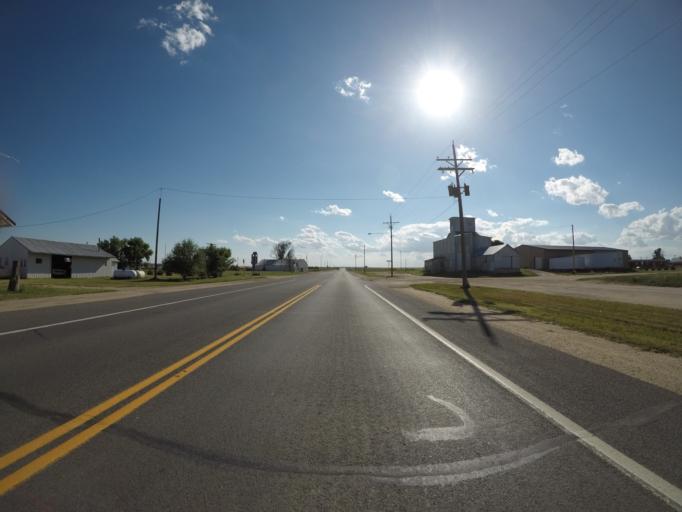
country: US
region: Colorado
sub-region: Morgan County
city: Fort Morgan
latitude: 40.6063
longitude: -103.8433
